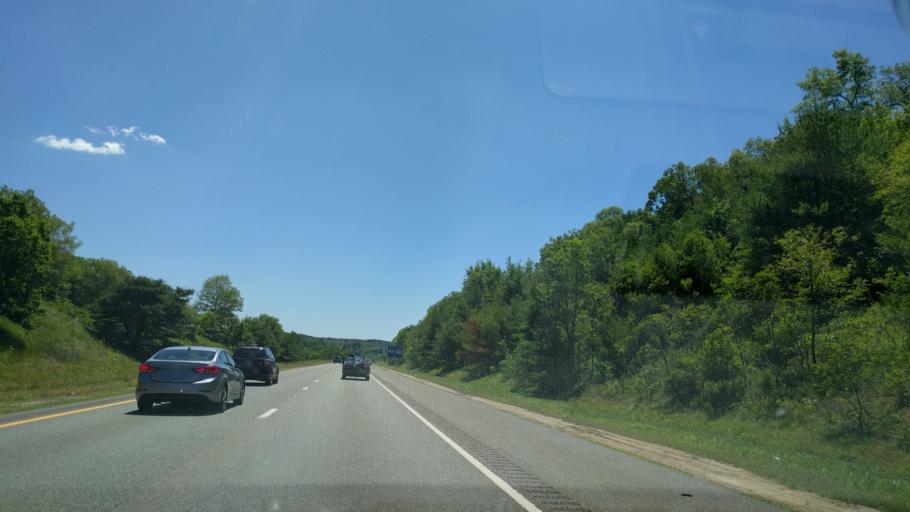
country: US
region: Massachusetts
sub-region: Worcester County
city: East Douglas
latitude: 42.0948
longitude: -71.6999
